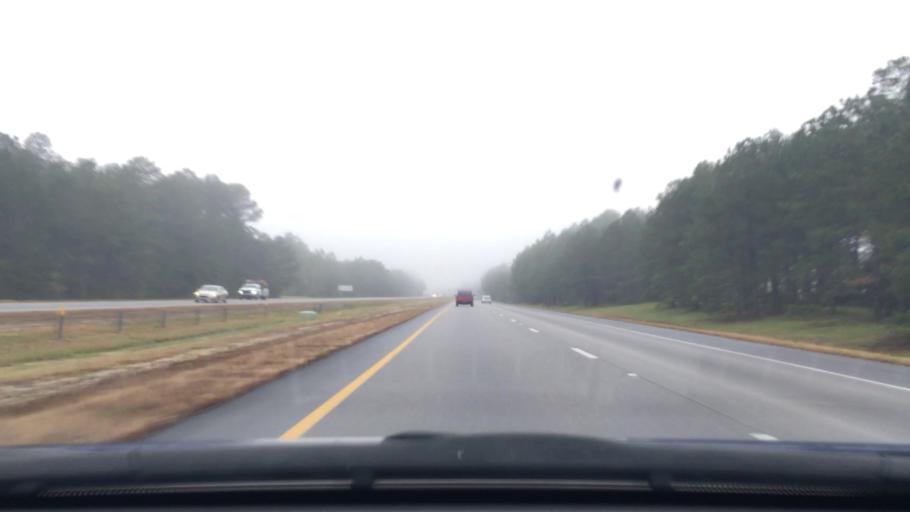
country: US
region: South Carolina
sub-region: Lee County
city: Bishopville
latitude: 34.2099
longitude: -80.4025
